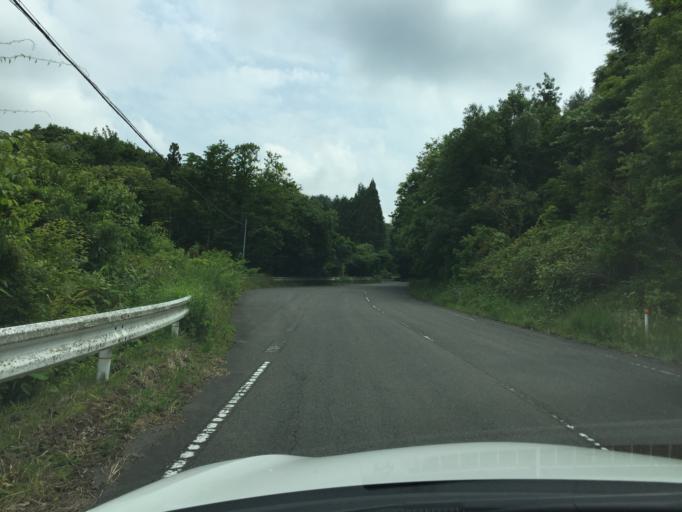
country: JP
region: Fukushima
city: Sukagawa
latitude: 37.2697
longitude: 140.5012
